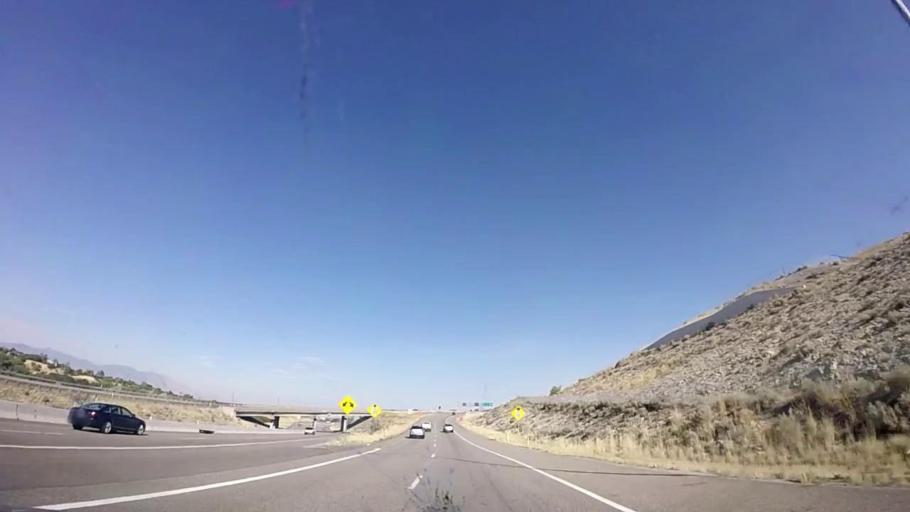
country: US
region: Utah
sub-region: Salt Lake County
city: East Millcreek
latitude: 40.7113
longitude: -111.8021
